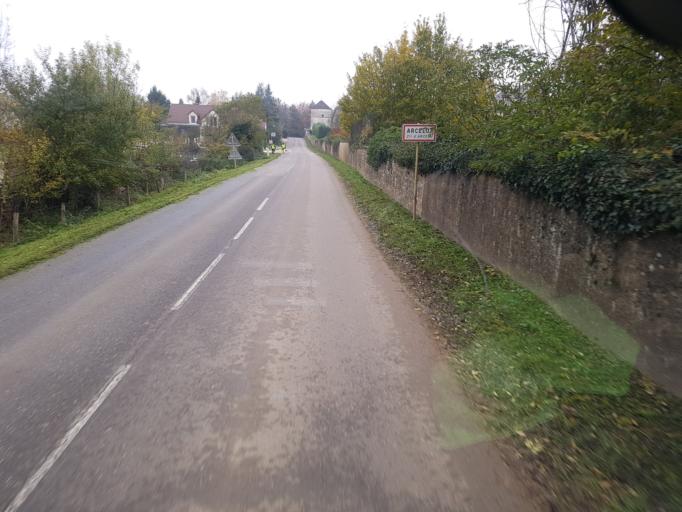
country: FR
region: Bourgogne
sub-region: Departement de la Cote-d'Or
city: Arc-sur-Tille
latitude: 47.3680
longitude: 5.1958
